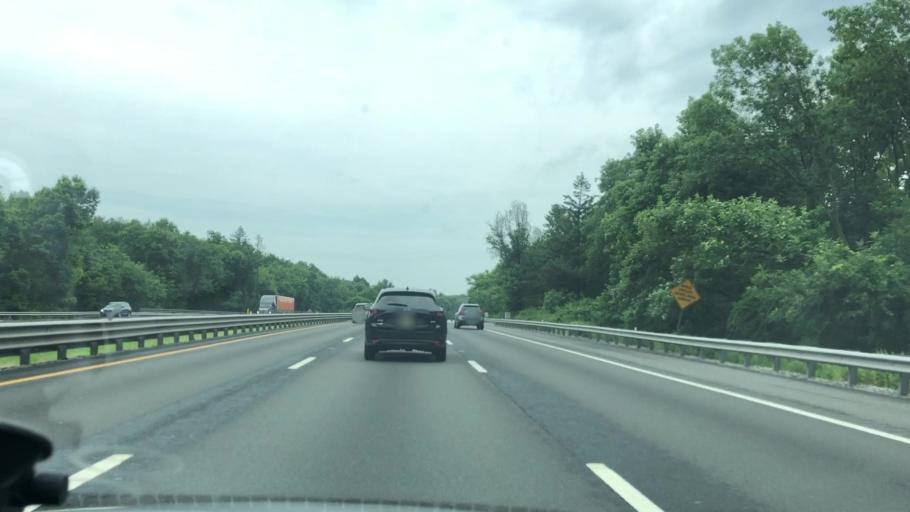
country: US
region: New Jersey
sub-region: Essex County
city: Fairfield
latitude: 40.8772
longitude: -74.3276
